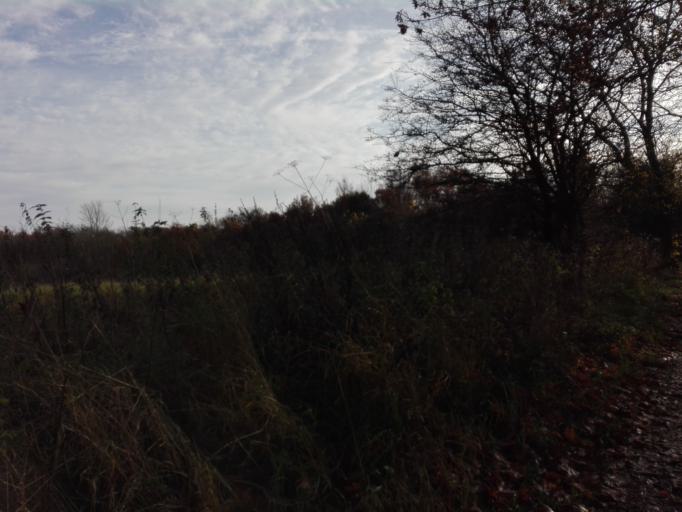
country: DK
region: Central Jutland
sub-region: Arhus Kommune
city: Beder
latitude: 56.0889
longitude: 10.2253
